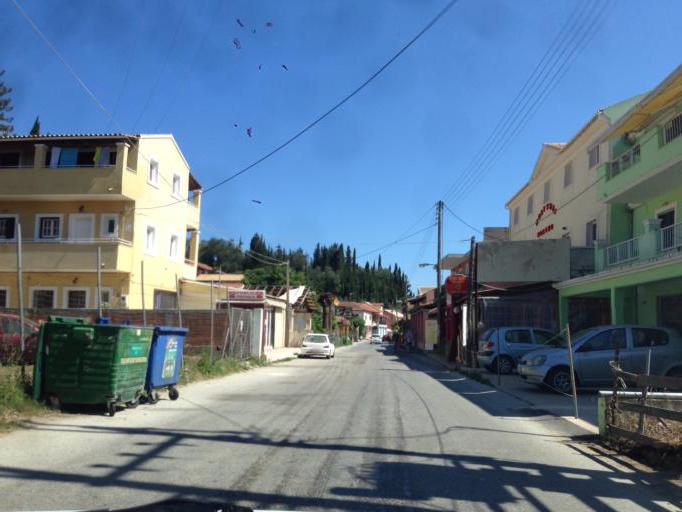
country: GR
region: Ionian Islands
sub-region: Nomos Kerkyras
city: Agios Georgis
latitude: 39.7874
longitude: 19.7084
